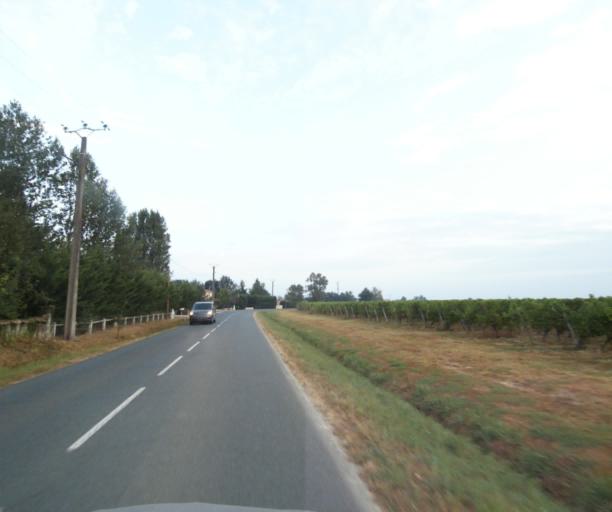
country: FR
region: Aquitaine
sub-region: Departement de la Gironde
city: La Sauve
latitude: 44.7646
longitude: -0.3332
